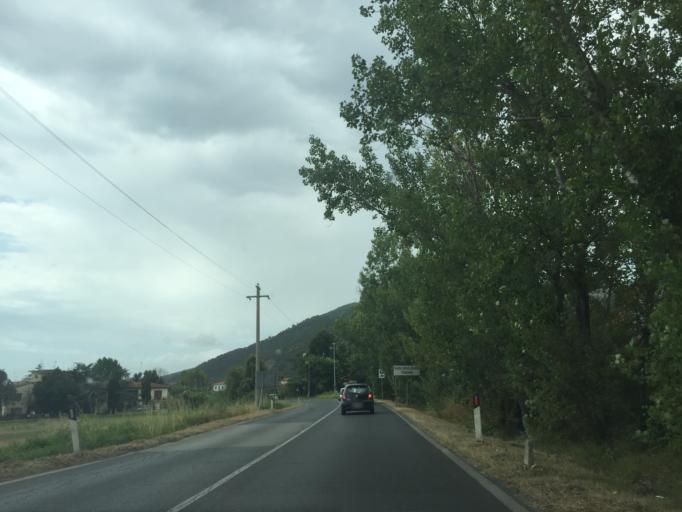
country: IT
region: Tuscany
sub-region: Province of Pisa
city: San Giuliano Terme
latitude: 43.7567
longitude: 10.4439
